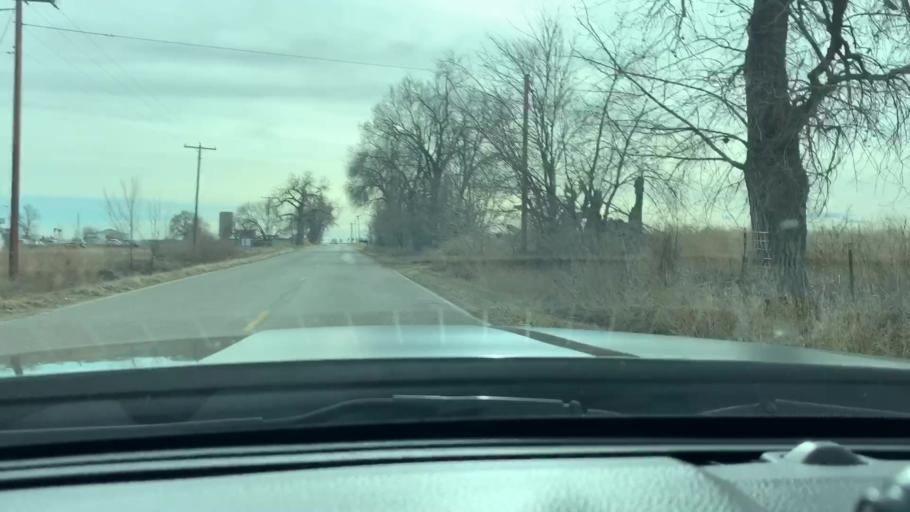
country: US
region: Colorado
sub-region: Weld County
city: Johnstown
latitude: 40.3530
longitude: -104.9835
